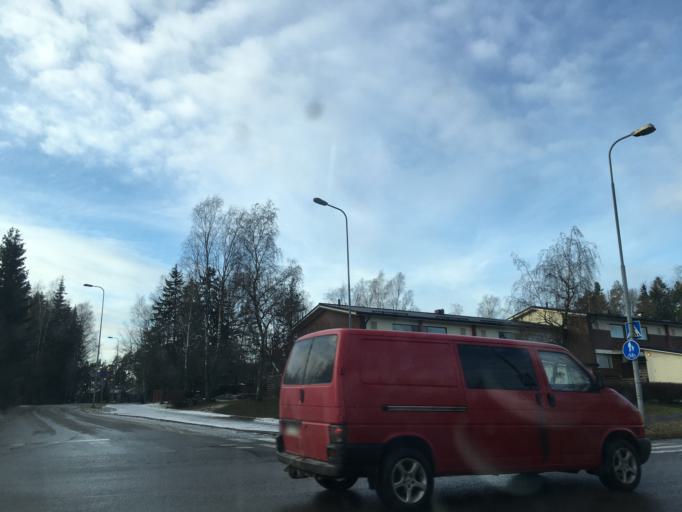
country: FI
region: Varsinais-Suomi
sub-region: Turku
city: Raisio
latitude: 60.4644
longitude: 22.1544
